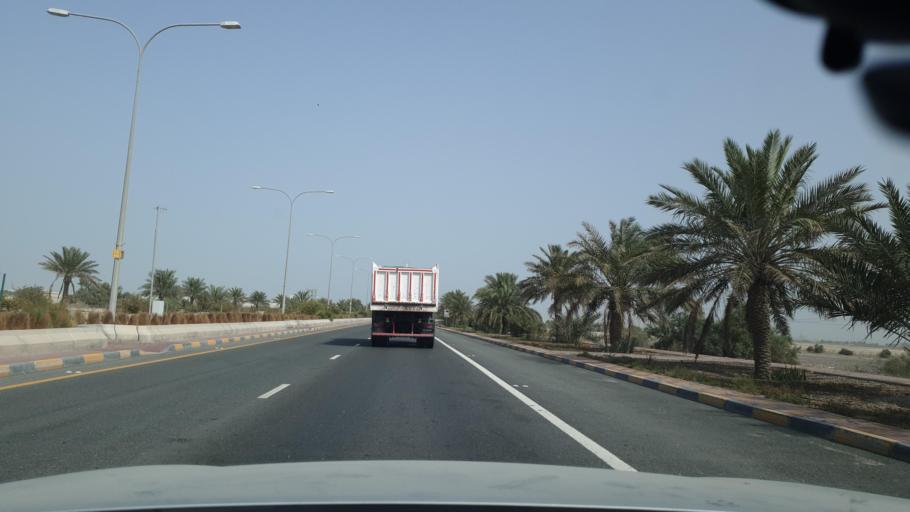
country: QA
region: Al Wakrah
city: Umm Sa'id
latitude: 25.0109
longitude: 51.5561
